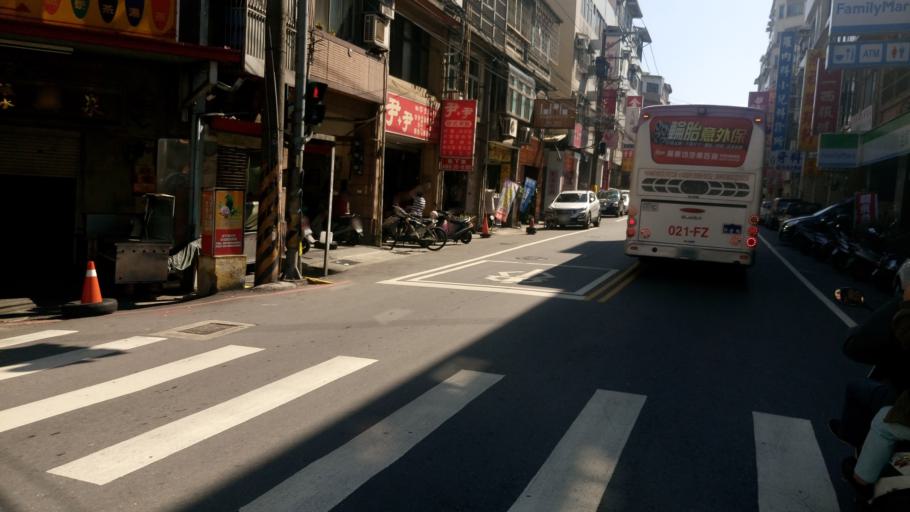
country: TW
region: Taiwan
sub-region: Hsinchu
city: Zhubei
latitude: 24.7378
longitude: 121.0875
